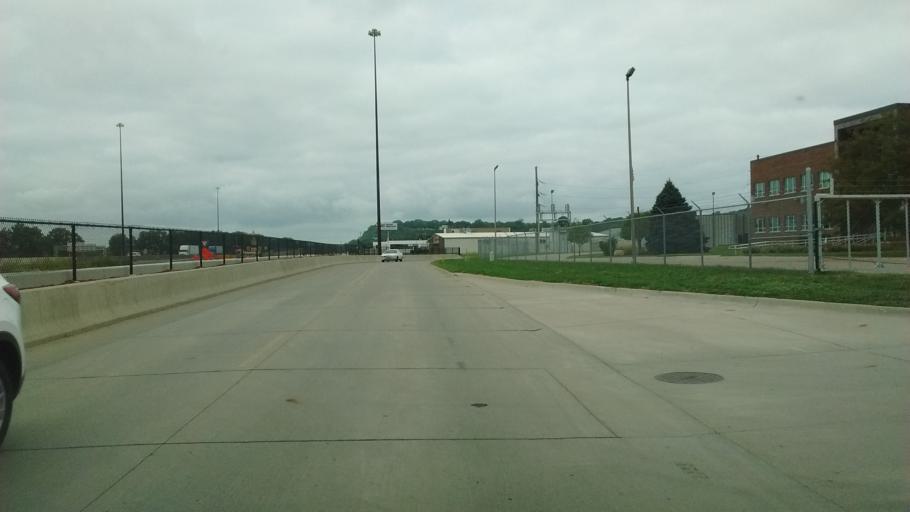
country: US
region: Nebraska
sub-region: Dakota County
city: South Sioux City
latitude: 42.4925
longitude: -96.4187
